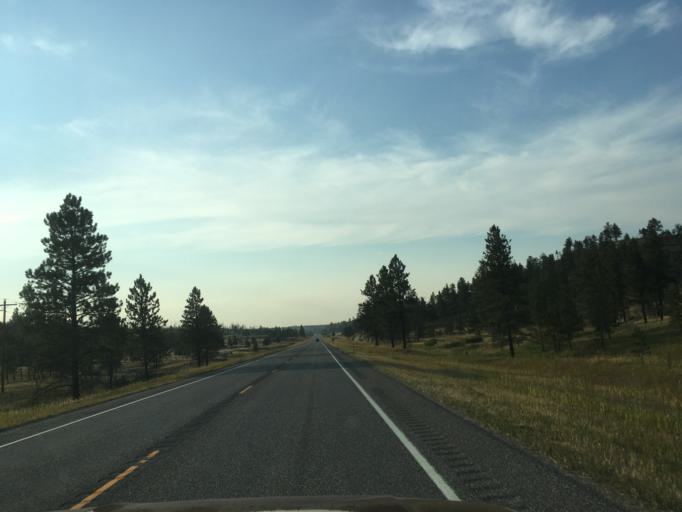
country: US
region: Montana
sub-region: Musselshell County
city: Roundup
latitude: 46.2817
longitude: -108.4772
